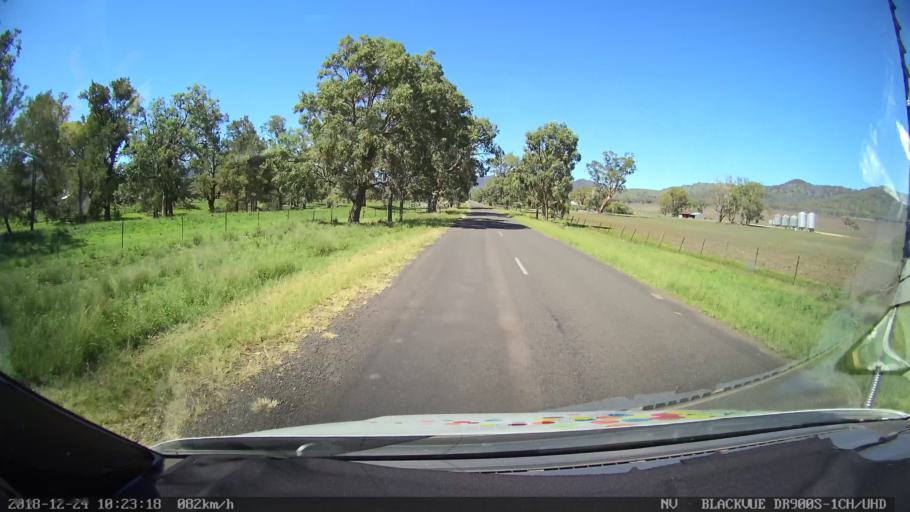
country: AU
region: New South Wales
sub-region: Liverpool Plains
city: Quirindi
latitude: -31.7736
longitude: 150.5390
